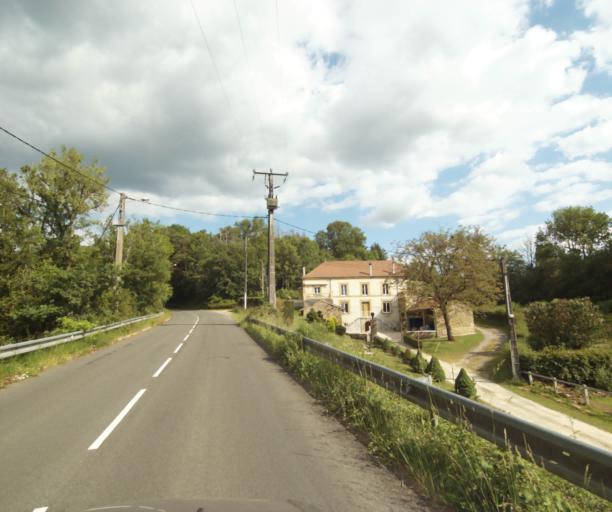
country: FR
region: Champagne-Ardenne
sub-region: Departement des Ardennes
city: Montcy-Notre-Dame
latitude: 49.7690
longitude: 4.7437
